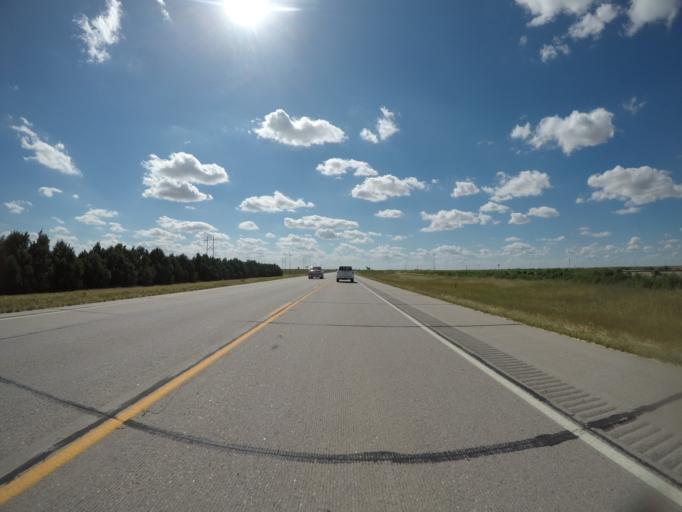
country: US
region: Colorado
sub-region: Phillips County
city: Holyoke
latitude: 40.5998
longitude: -102.3966
